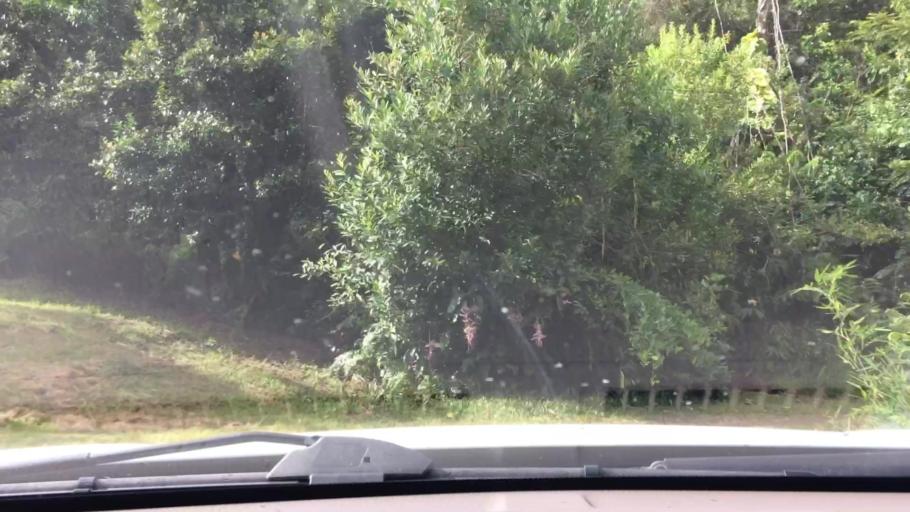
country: US
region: Hawaii
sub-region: Hawaii County
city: Pepeekeo
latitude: 19.8257
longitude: -155.1140
